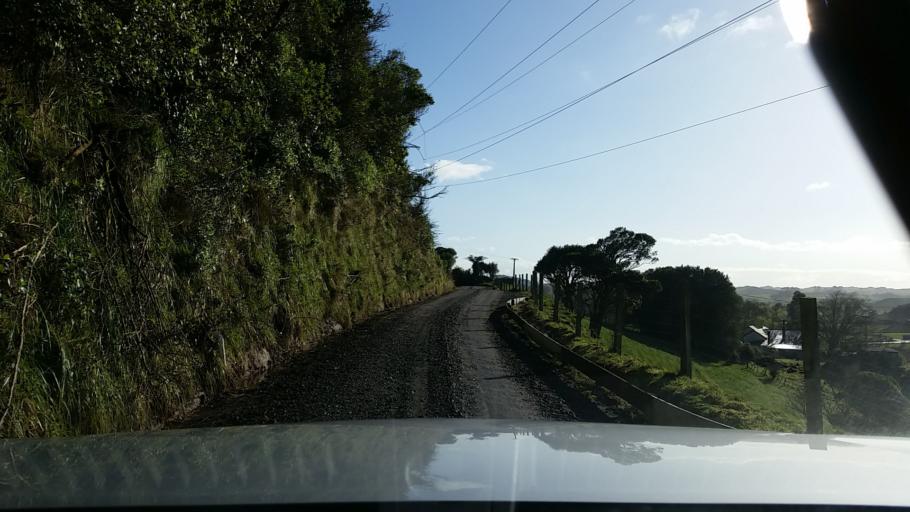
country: NZ
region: Taranaki
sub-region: South Taranaki District
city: Eltham
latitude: -39.4545
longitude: 174.3685
